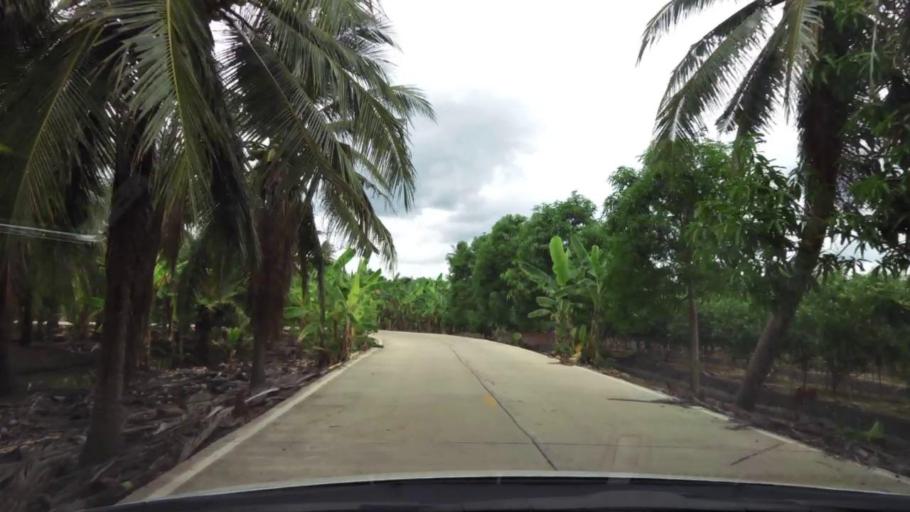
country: TH
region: Samut Sakhon
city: Ban Phaeo
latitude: 13.5587
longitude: 100.0294
